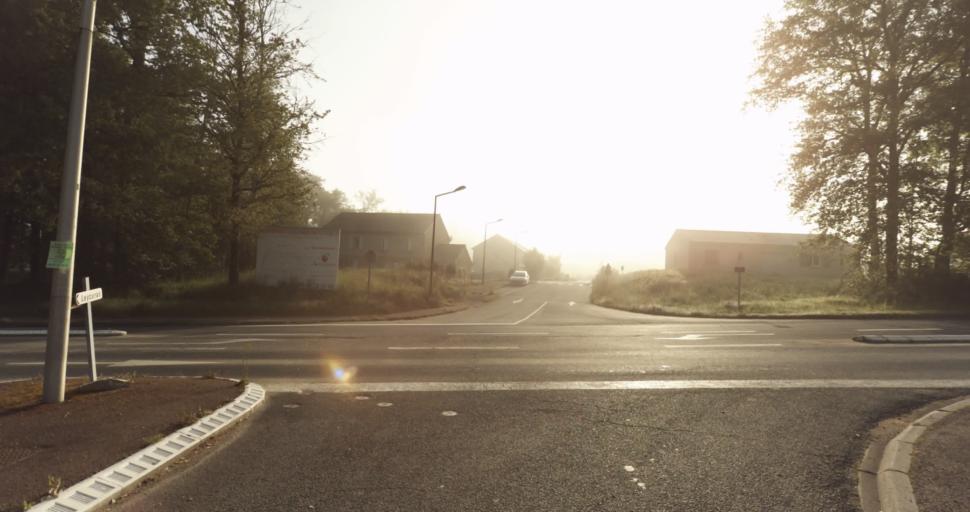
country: FR
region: Limousin
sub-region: Departement de la Haute-Vienne
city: Condat-sur-Vienne
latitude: 45.7884
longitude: 1.2855
